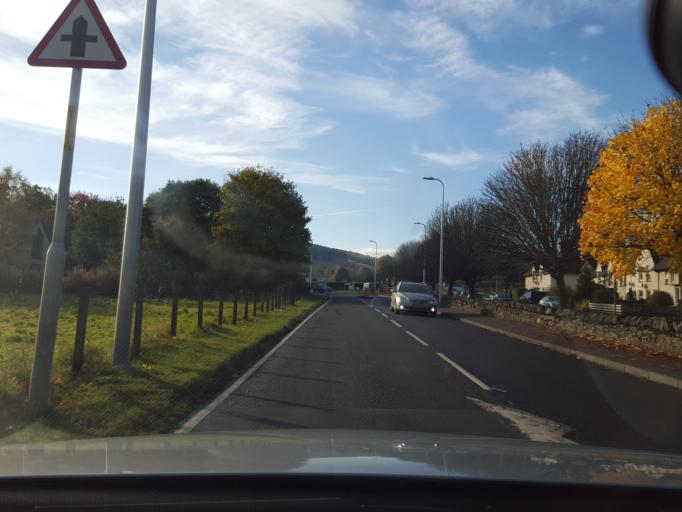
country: GB
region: Scotland
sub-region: Highland
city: Beauly
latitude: 57.3332
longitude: -4.4805
